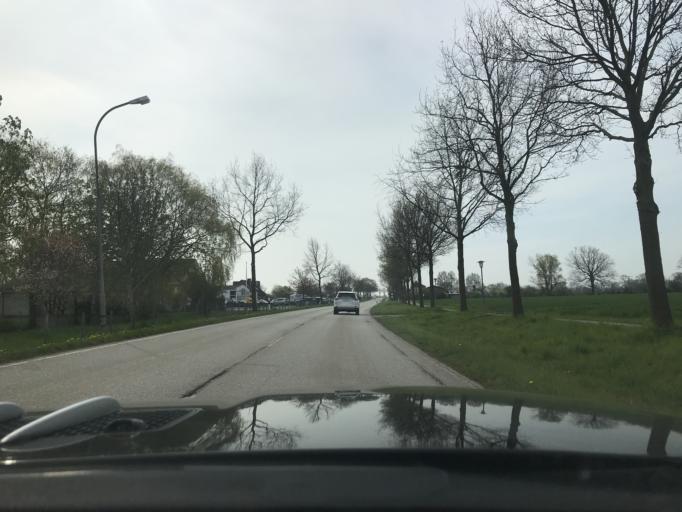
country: DE
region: Schleswig-Holstein
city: Heringsdorf
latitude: 54.2751
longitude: 11.0326
